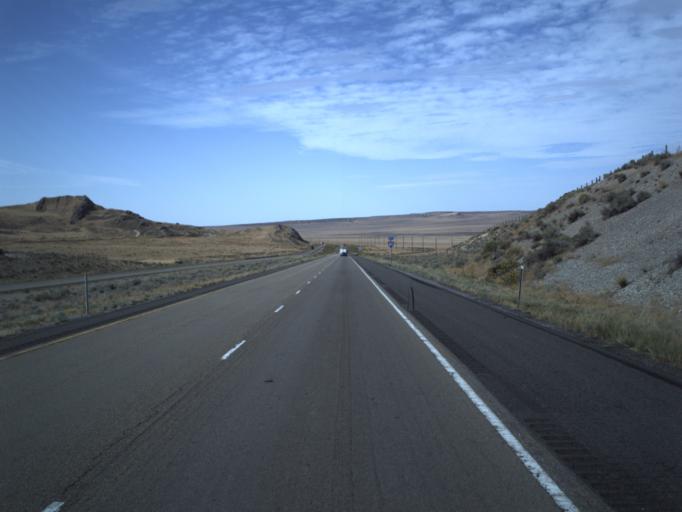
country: US
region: Utah
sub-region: Tooele County
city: Grantsville
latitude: 40.8194
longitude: -112.9096
